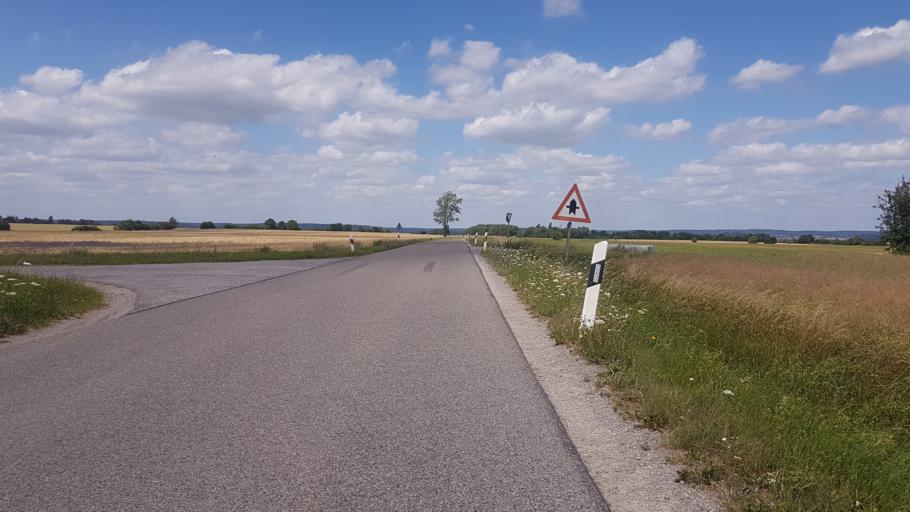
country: DE
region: Bavaria
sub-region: Regierungsbezirk Mittelfranken
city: Geslau
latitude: 49.3338
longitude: 10.3347
